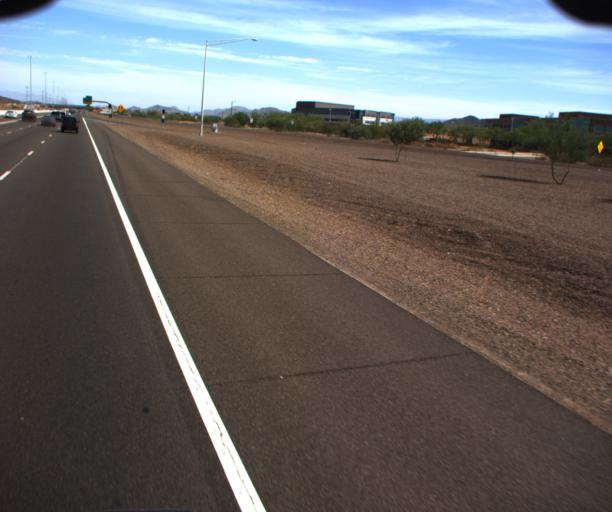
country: US
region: Arizona
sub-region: Maricopa County
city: Anthem
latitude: 33.7150
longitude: -112.1177
